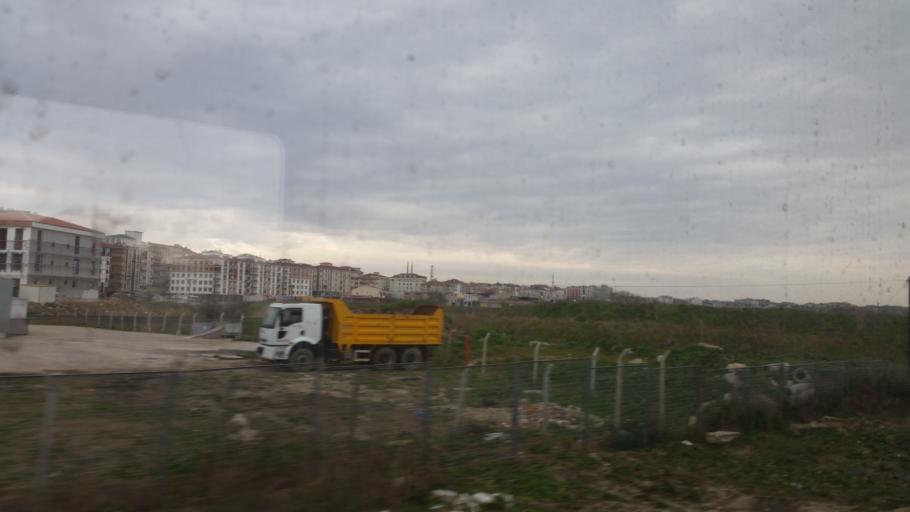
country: TR
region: Tekirdag
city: Cerkezkoey
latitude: 41.2774
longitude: 27.9880
